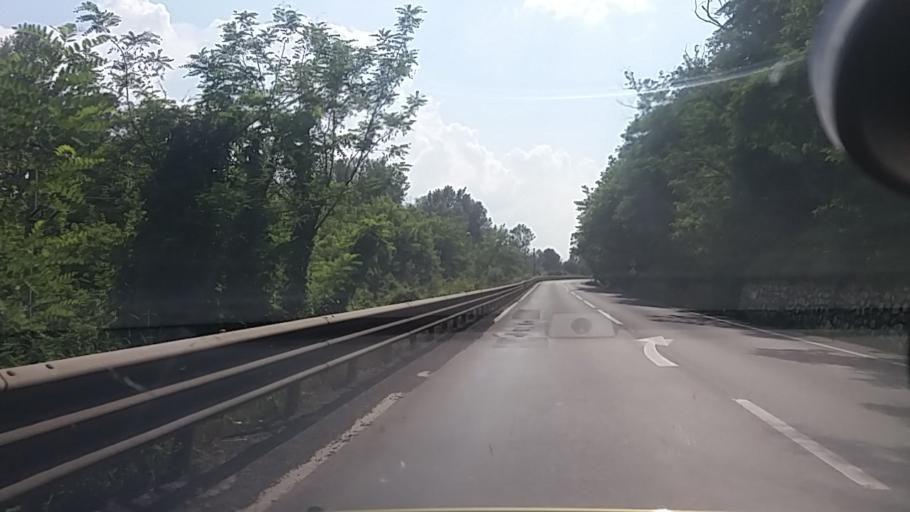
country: RO
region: Arad
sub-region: Comuna Savarsin
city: Savarsin
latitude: 46.0062
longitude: 22.2097
